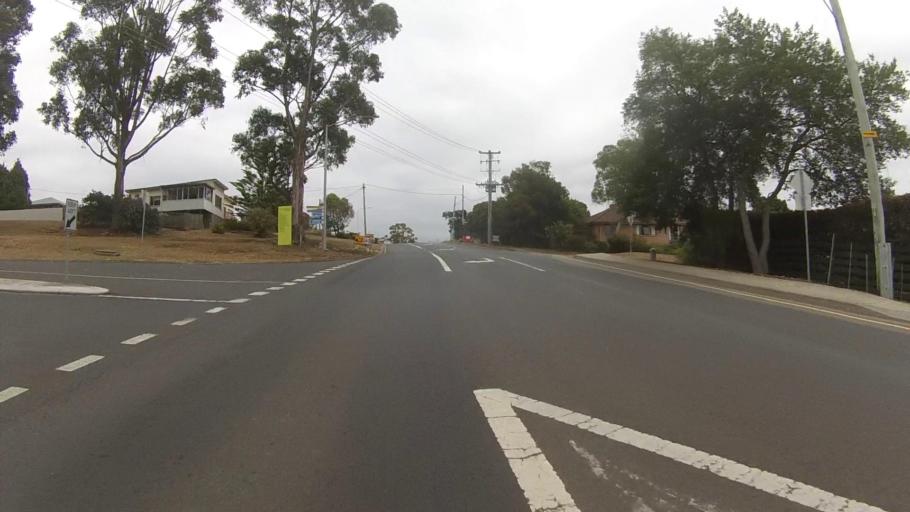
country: AU
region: Tasmania
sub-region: Kingborough
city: Kingston
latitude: -42.9690
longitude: 147.2902
